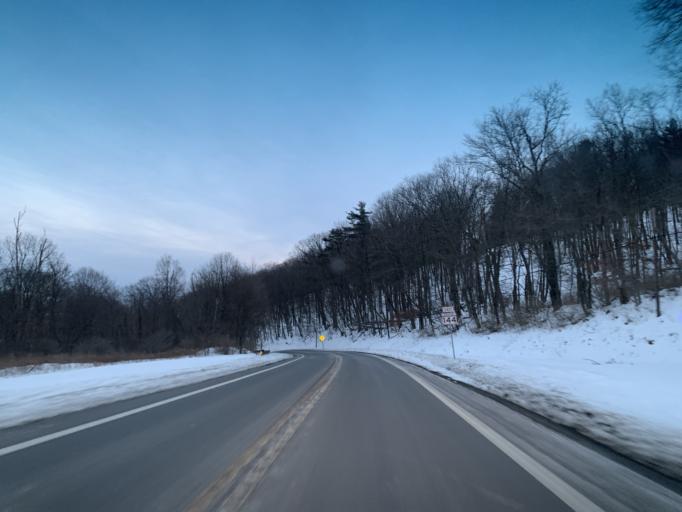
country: US
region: Maryland
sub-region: Allegany County
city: Cumberland
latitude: 39.6956
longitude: -78.5204
